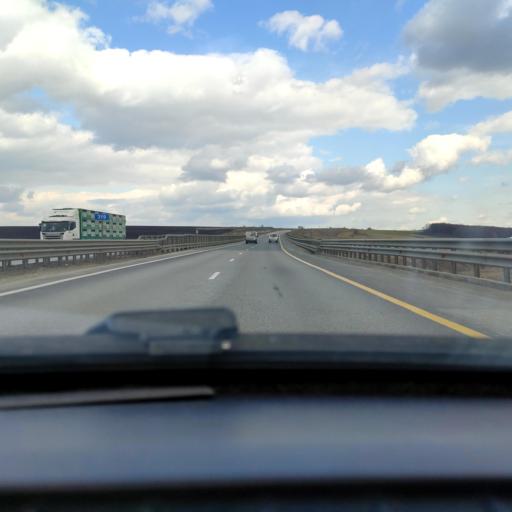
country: RU
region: Tula
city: Yefremov
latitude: 53.1135
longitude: 38.1947
